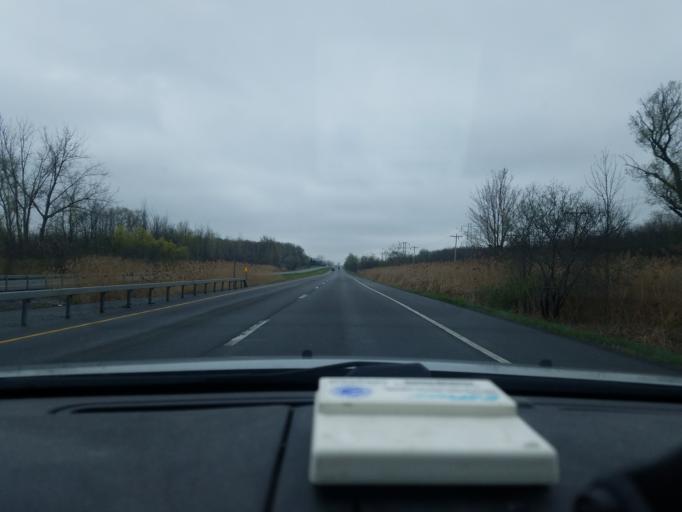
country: US
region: New York
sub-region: Onondaga County
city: East Syracuse
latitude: 43.1146
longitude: -76.0790
